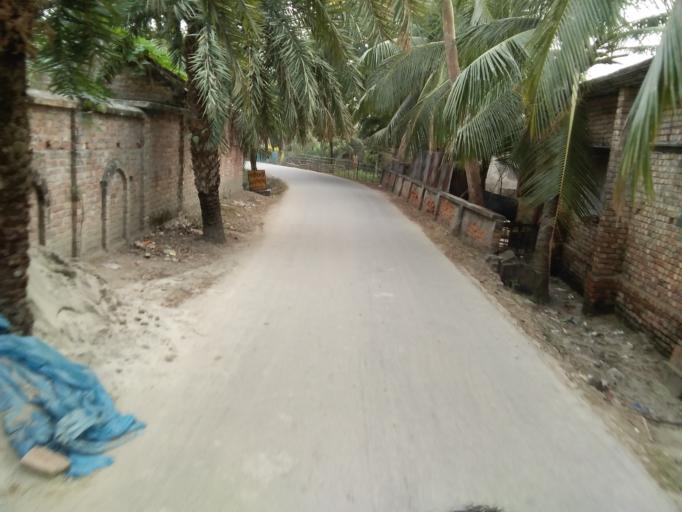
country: BD
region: Khulna
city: Satkhira
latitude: 22.5862
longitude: 89.0620
